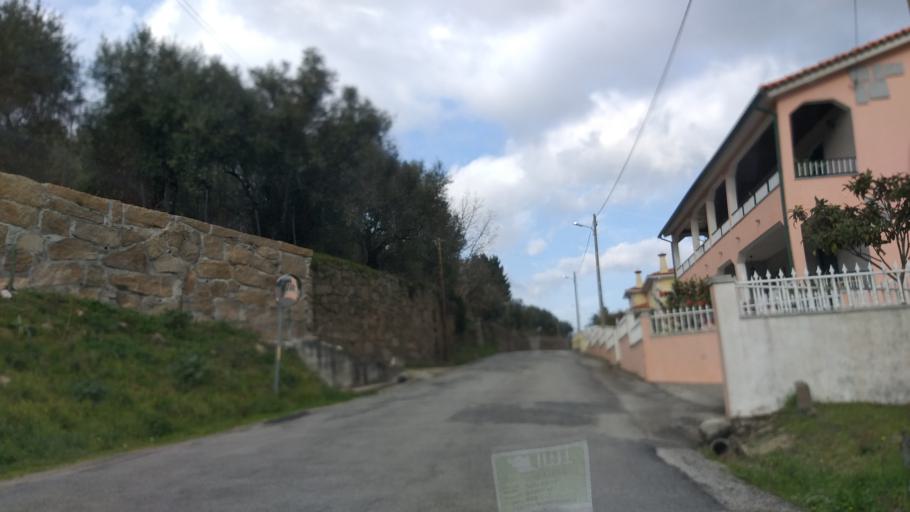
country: PT
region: Guarda
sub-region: Seia
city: Seia
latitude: 40.4642
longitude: -7.6889
